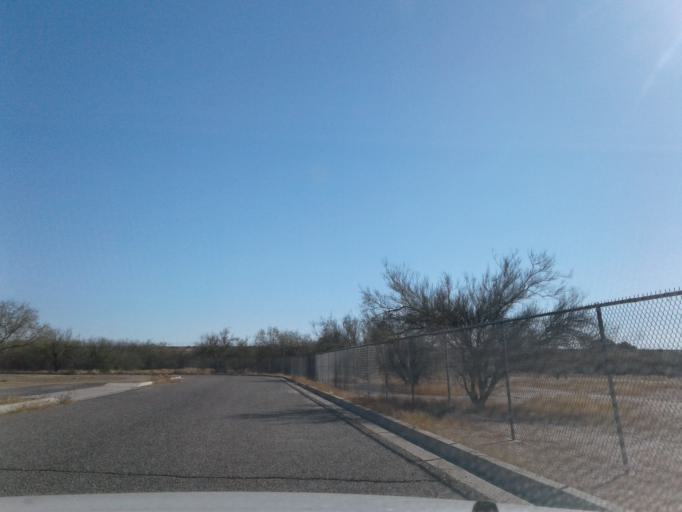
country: US
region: Arizona
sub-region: Maricopa County
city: Paradise Valley
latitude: 33.6635
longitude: -111.9891
